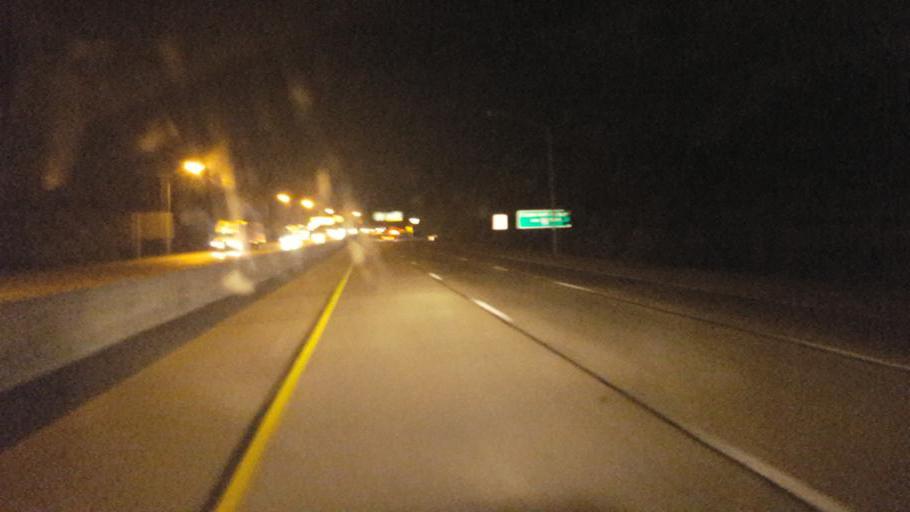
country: US
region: Indiana
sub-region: Marion County
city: Speedway
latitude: 39.7393
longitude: -86.2389
